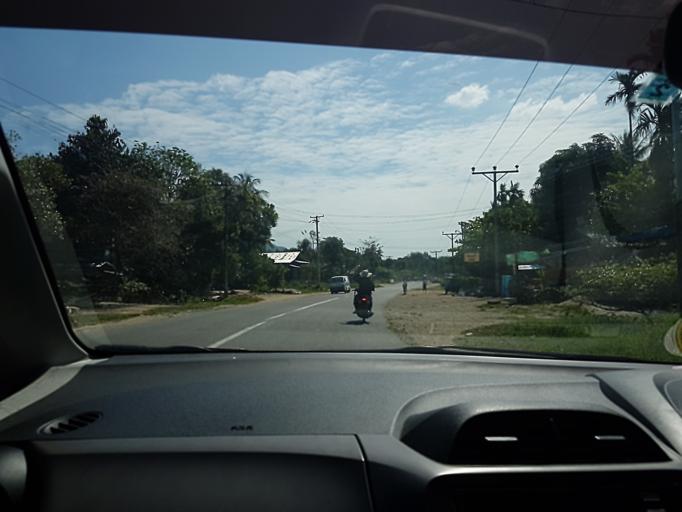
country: MM
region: Mon
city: Thaton
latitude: 16.7125
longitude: 97.4212
